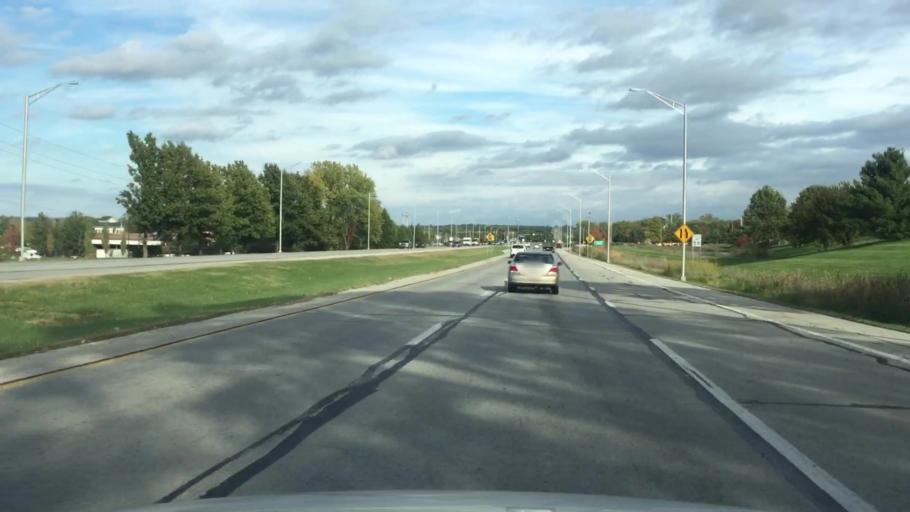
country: US
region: Kansas
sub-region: Wyandotte County
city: Edwardsville
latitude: 39.0074
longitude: -94.8440
